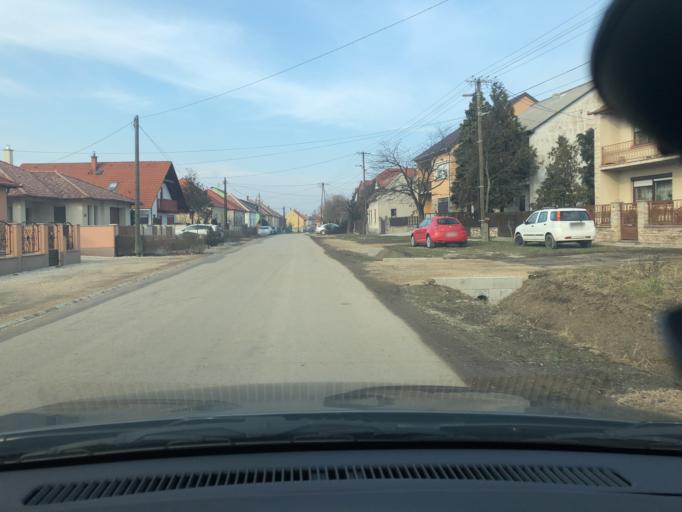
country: HU
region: Gyor-Moson-Sopron
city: Kapuvar
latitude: 47.5868
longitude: 17.0215
